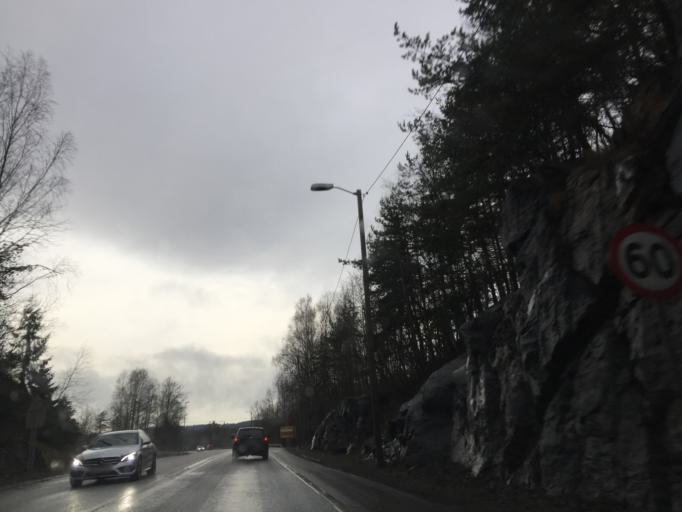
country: NO
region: Ostfold
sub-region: Moss
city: Moss
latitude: 59.4456
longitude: 10.6922
